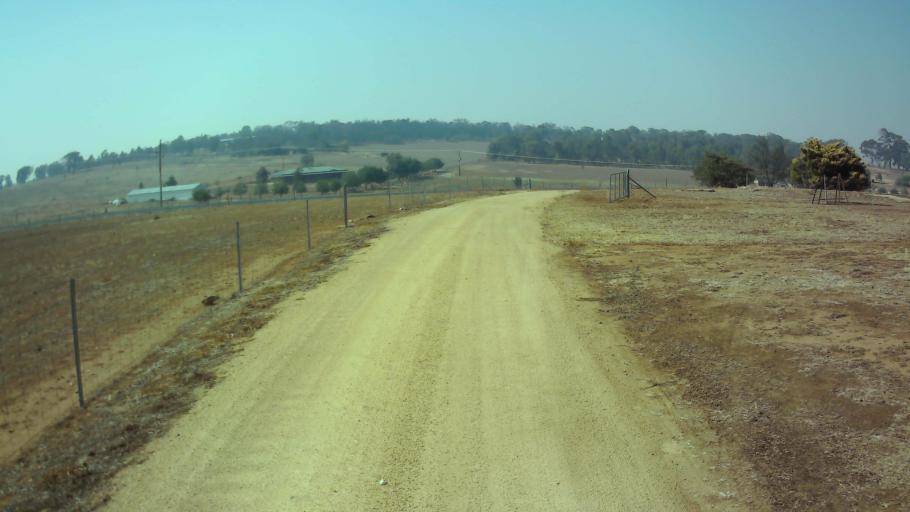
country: AU
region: New South Wales
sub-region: Weddin
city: Grenfell
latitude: -33.8979
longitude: 148.1797
